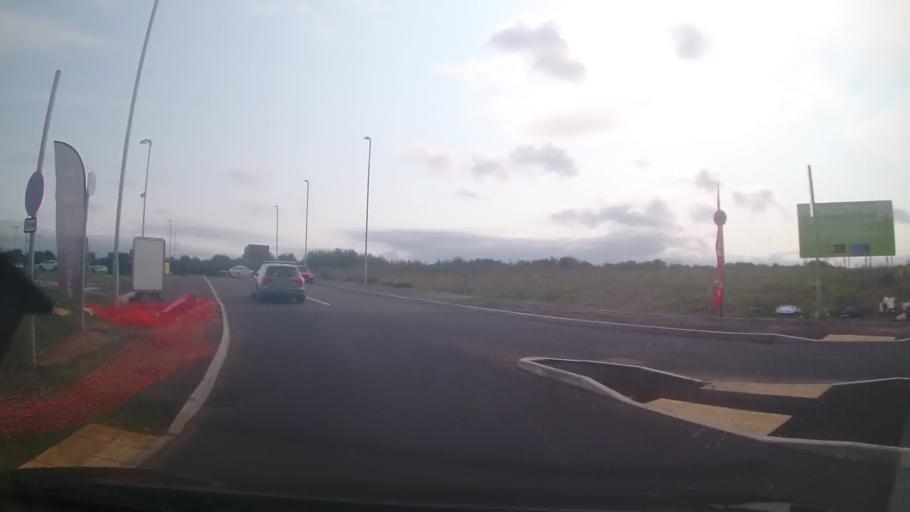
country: GB
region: England
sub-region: Shropshire
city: Shrewsbury
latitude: 52.6906
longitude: -2.7166
